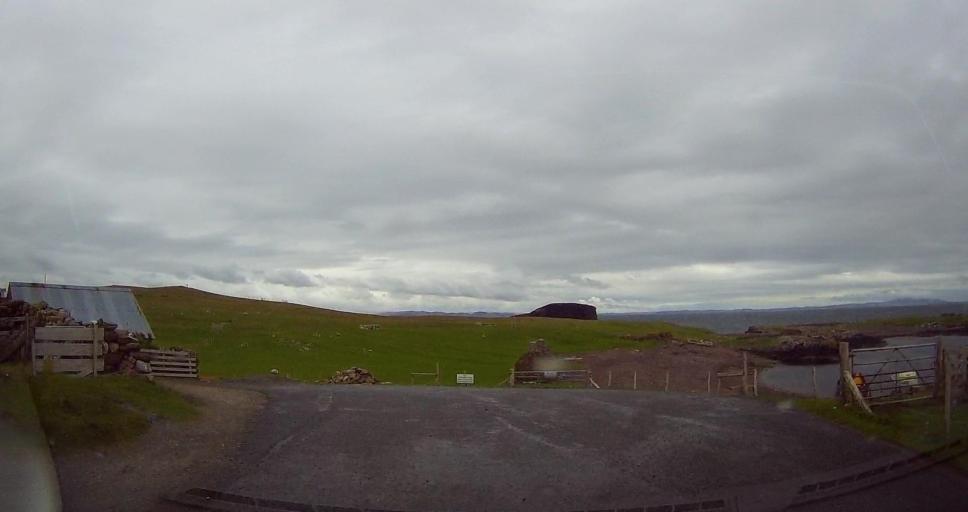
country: GB
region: Scotland
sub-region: Shetland Islands
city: Lerwick
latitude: 60.4784
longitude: -1.6131
